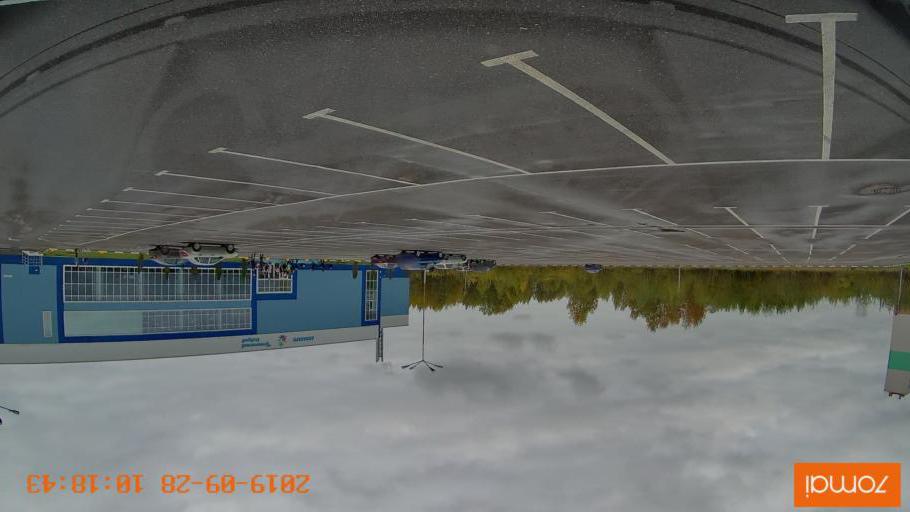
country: RU
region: Jaroslavl
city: Yaroslavl
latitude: 57.5705
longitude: 39.9175
